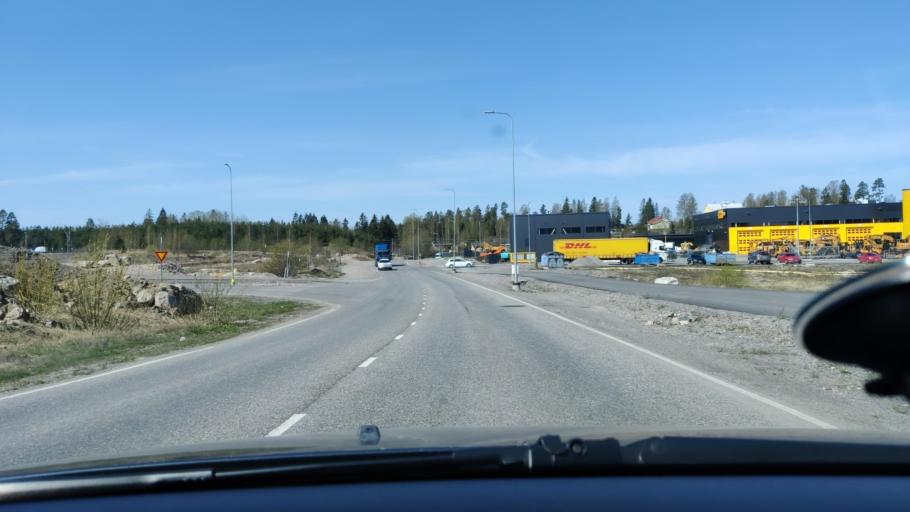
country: FI
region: Uusimaa
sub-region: Helsinki
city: Kerava
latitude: 60.3749
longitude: 25.1017
